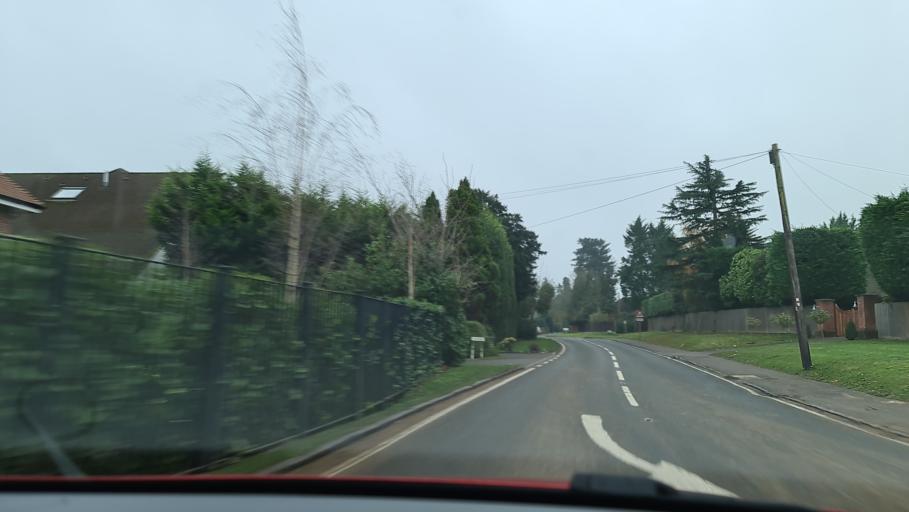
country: GB
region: England
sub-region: Buckinghamshire
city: Beaconsfield
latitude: 51.6282
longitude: -0.6557
